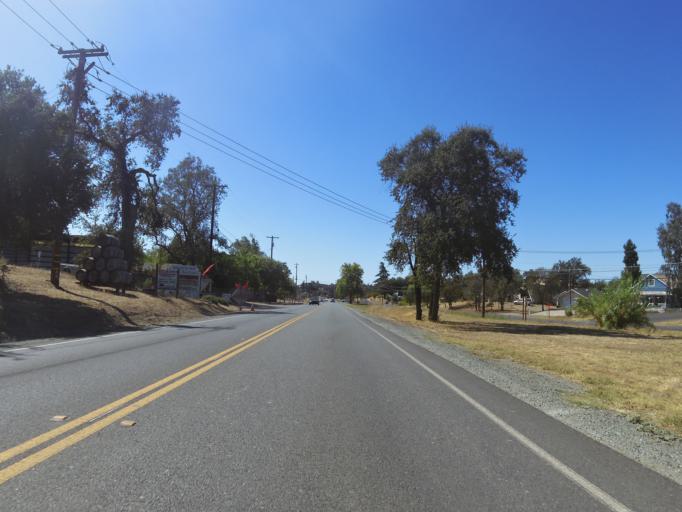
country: US
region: California
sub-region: Amador County
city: Plymouth
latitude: 38.4799
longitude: -120.8461
